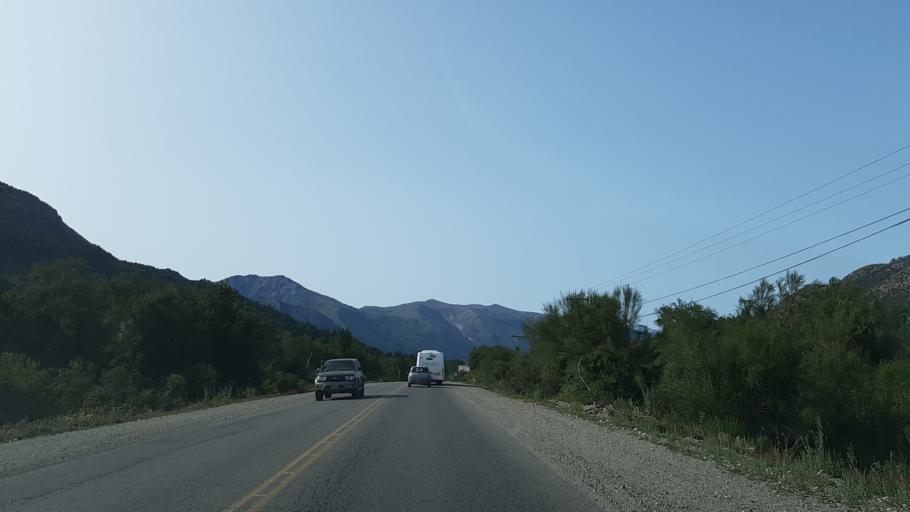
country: AR
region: Rio Negro
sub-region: Departamento de Bariloche
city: San Carlos de Bariloche
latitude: -41.1414
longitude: -71.4110
